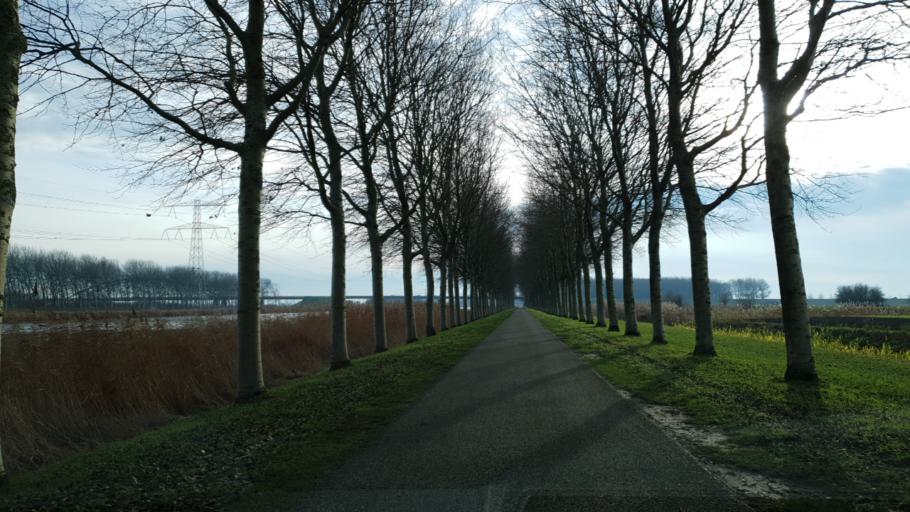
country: NL
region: North Brabant
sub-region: Gemeente Woensdrecht
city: Woensdrecht
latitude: 51.4078
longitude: 4.2336
